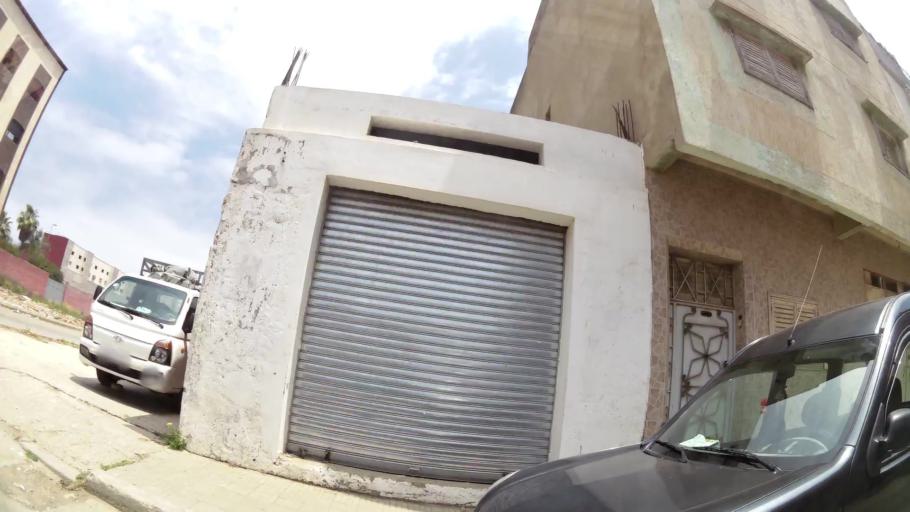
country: MA
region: Rabat-Sale-Zemmour-Zaer
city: Sale
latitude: 34.0541
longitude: -6.7872
